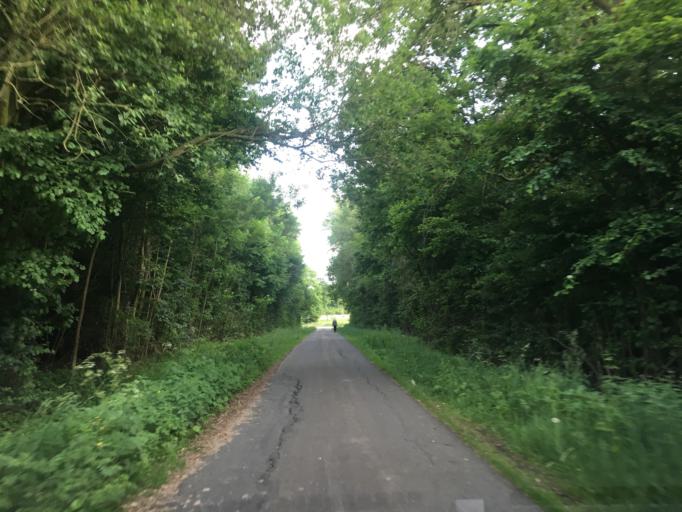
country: DE
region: North Rhine-Westphalia
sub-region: Regierungsbezirk Munster
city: Altenberge
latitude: 52.0225
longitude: 7.5418
